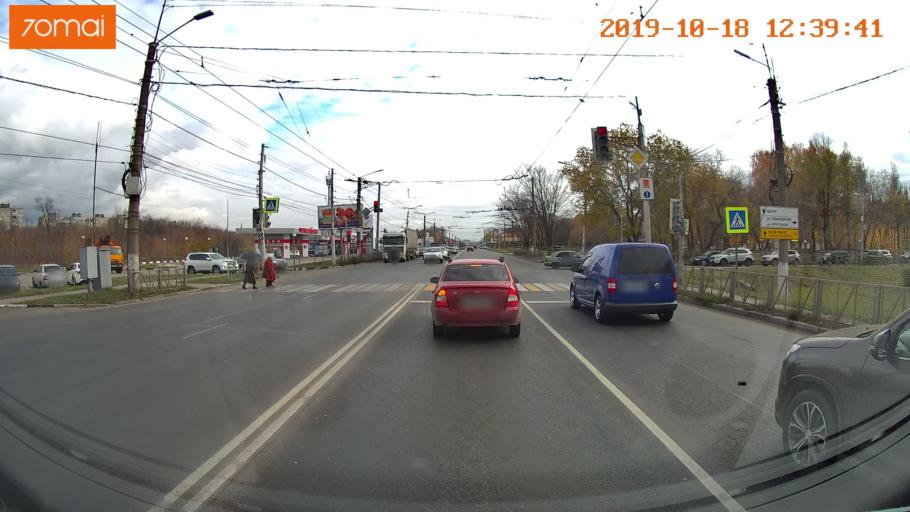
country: RU
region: Rjazan
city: Ryazan'
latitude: 54.6493
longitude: 39.6474
